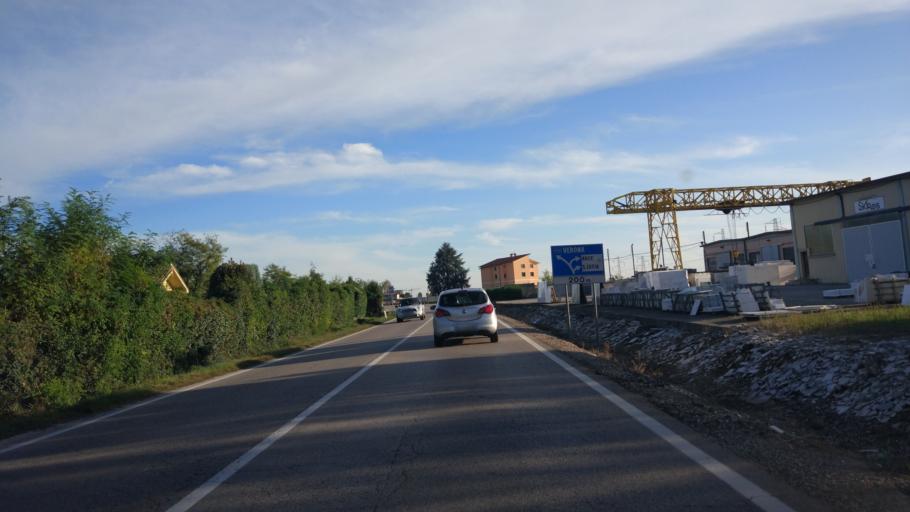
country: IT
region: Veneto
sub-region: Provincia di Verona
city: Sant'Ambrogio di Valpollicella
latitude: 45.5102
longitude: 10.8287
